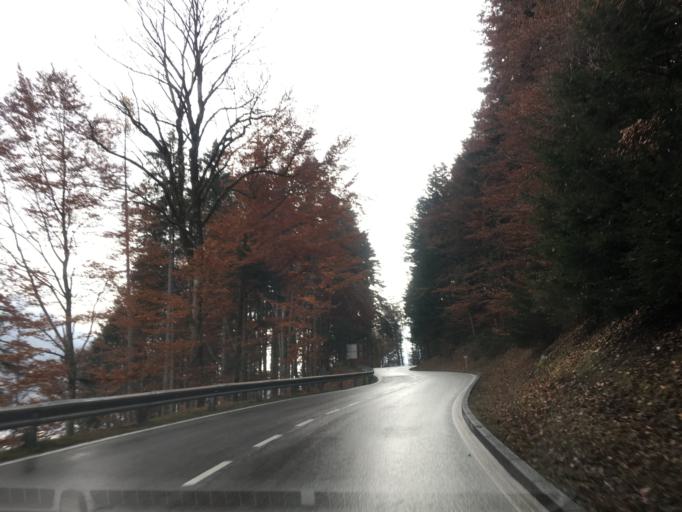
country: AT
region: Vorarlberg
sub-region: Politischer Bezirk Bludenz
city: Buers
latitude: 47.1534
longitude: 9.7945
